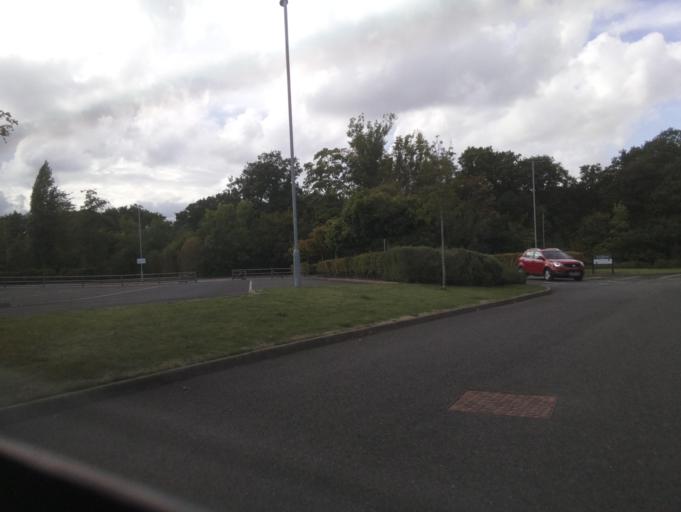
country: GB
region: England
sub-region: Staffordshire
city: Barlaston
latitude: 52.9561
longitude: -2.1707
